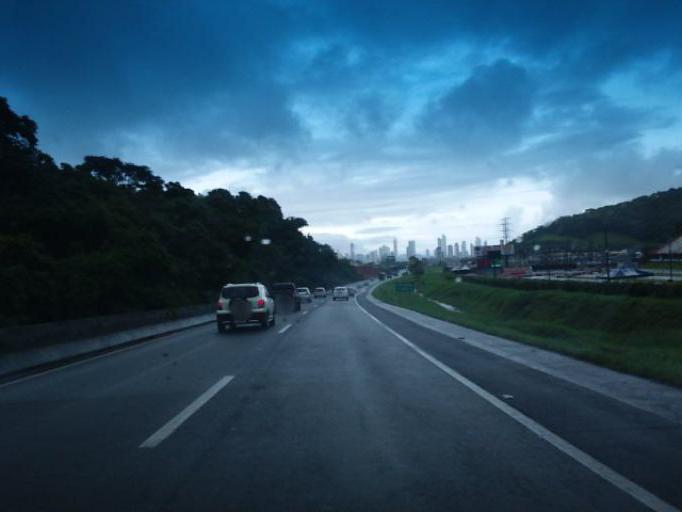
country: BR
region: Santa Catarina
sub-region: Itapema
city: Itapema
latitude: -27.0371
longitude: -48.6035
